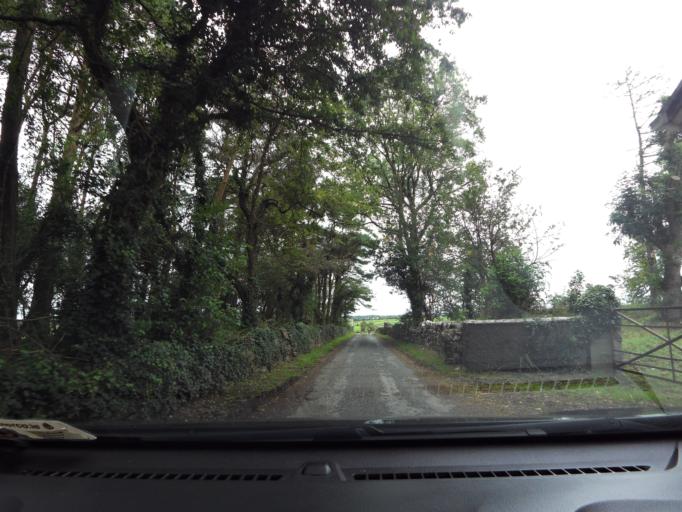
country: IE
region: Connaught
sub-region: County Galway
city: Athenry
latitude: 53.3124
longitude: -8.7454
